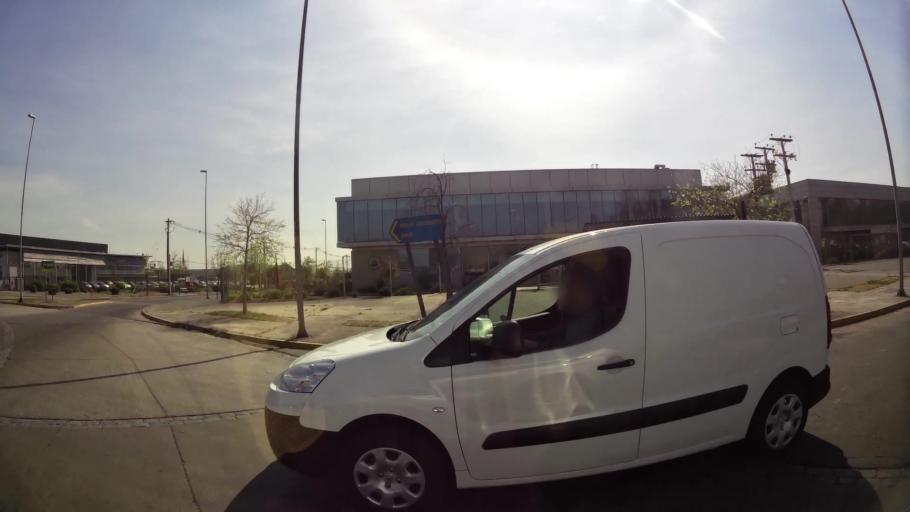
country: CL
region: Santiago Metropolitan
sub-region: Provincia de Santiago
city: Lo Prado
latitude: -33.4278
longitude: -70.7780
